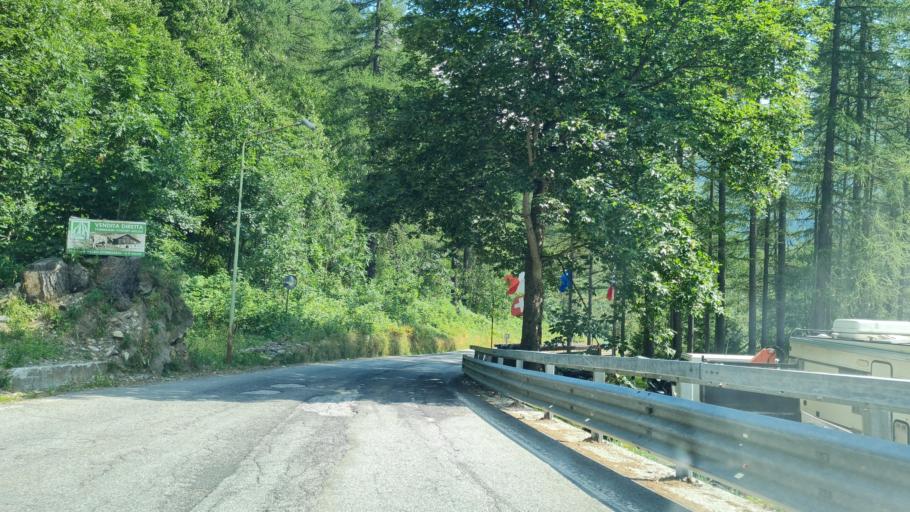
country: IT
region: Piedmont
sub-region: Provincia Verbano-Cusio-Ossola
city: Formazza
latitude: 46.3840
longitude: 8.4256
